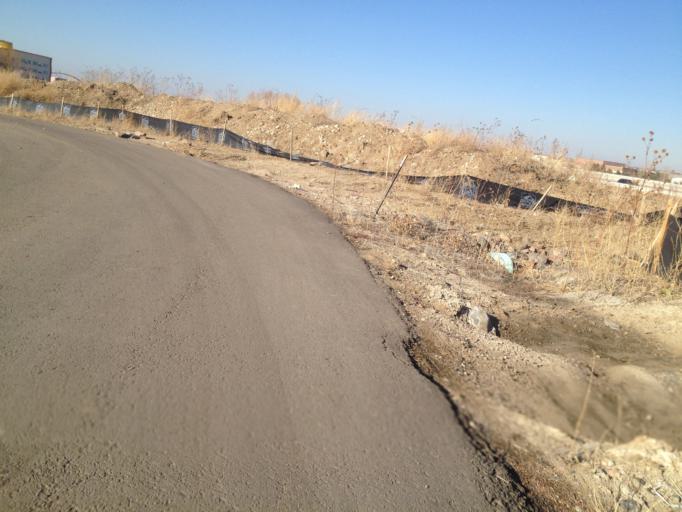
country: US
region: Colorado
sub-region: Boulder County
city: Superior
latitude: 39.9536
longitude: -105.1601
